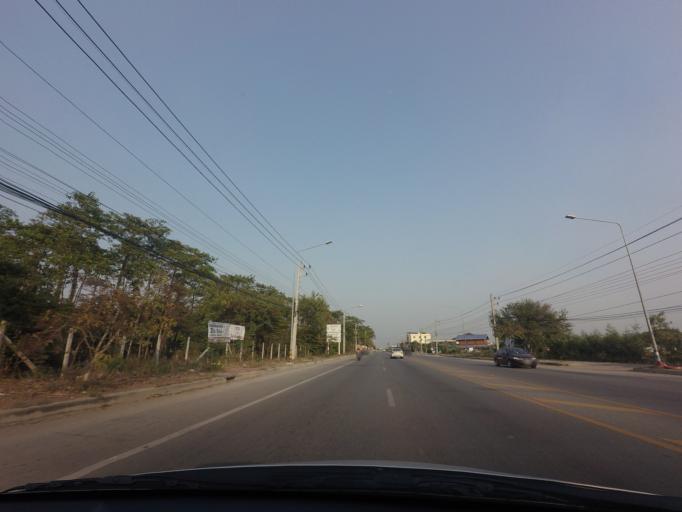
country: TH
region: Nakhon Pathom
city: Nakhon Chai Si
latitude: 13.8046
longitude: 100.2268
